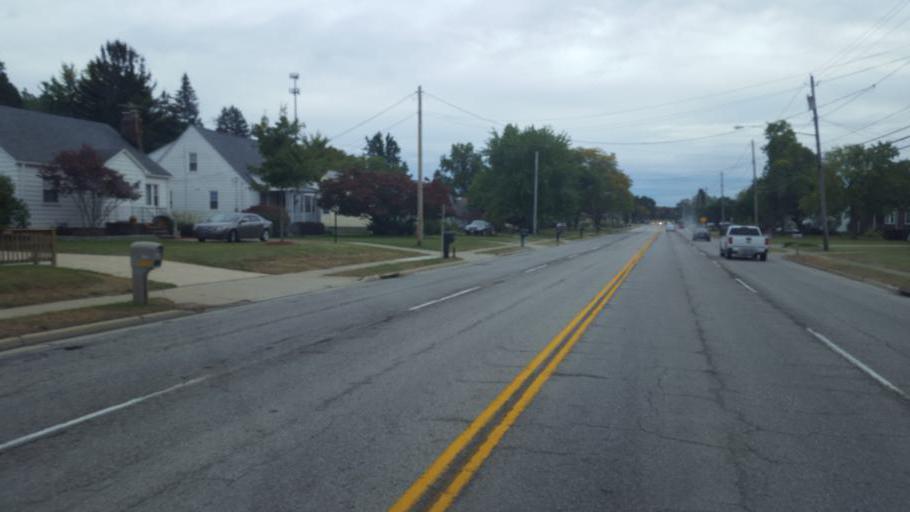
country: US
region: Ohio
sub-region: Lorain County
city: Lorain
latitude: 41.4212
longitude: -82.1628
